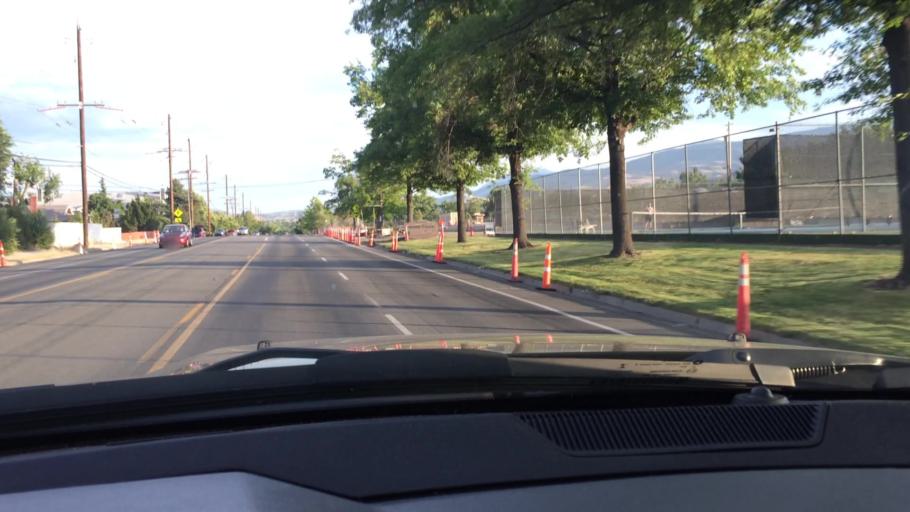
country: US
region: Nevada
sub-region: Washoe County
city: Reno
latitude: 39.4993
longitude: -119.8127
